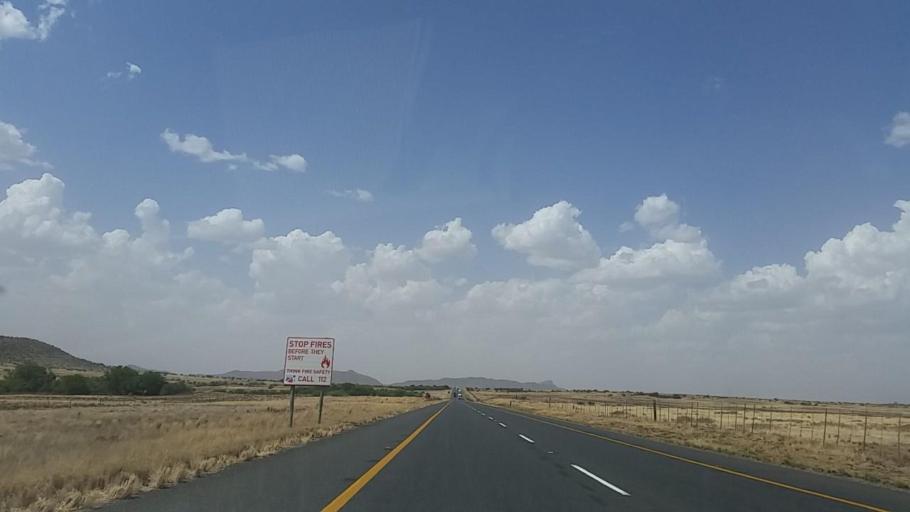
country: ZA
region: Northern Cape
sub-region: Pixley ka Seme District Municipality
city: Colesberg
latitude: -30.5780
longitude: 25.4367
